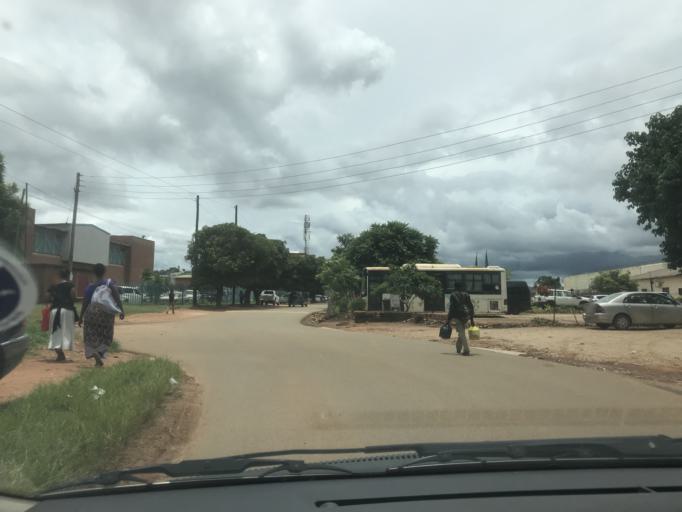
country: ZM
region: Lusaka
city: Lusaka
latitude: -15.4312
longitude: 28.3084
